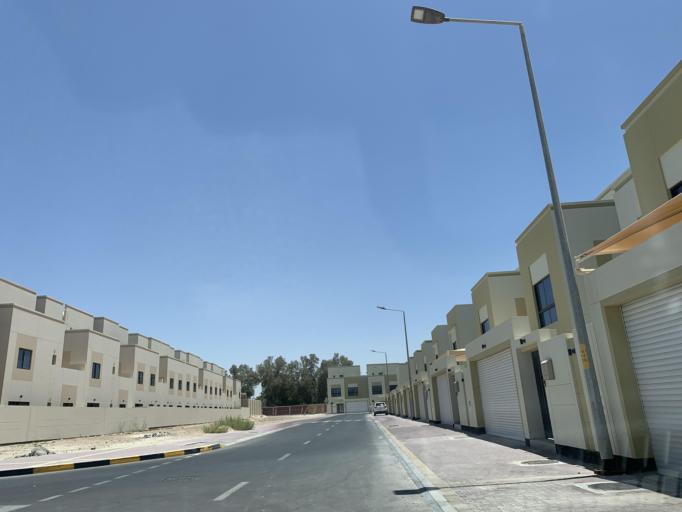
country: BH
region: Manama
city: Jidd Hafs
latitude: 26.2327
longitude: 50.4965
